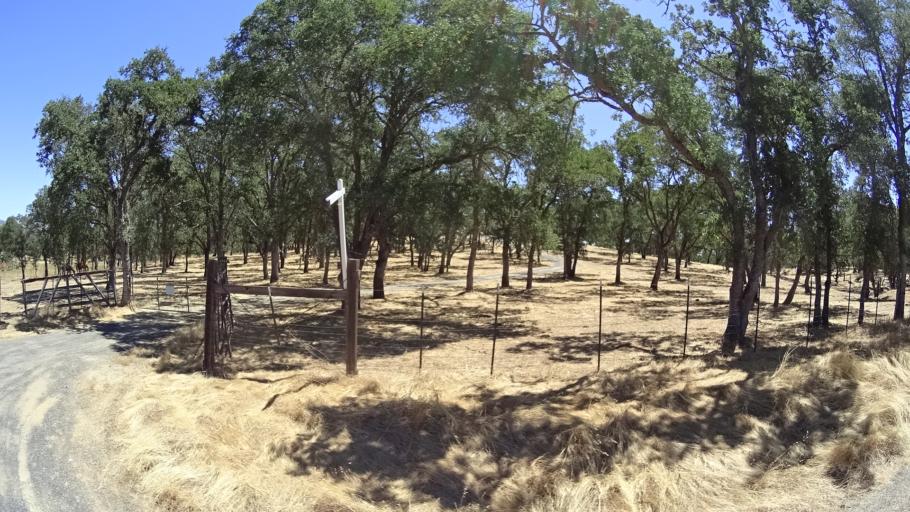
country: US
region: California
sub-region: Calaveras County
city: Copperopolis
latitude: 37.9793
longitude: -120.7017
